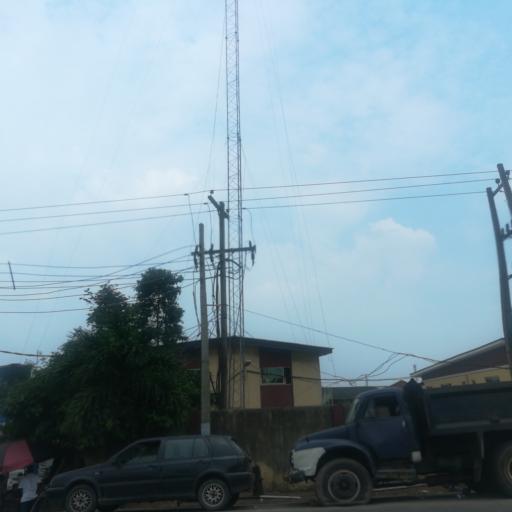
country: NG
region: Lagos
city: Ojota
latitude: 6.5829
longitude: 3.3846
